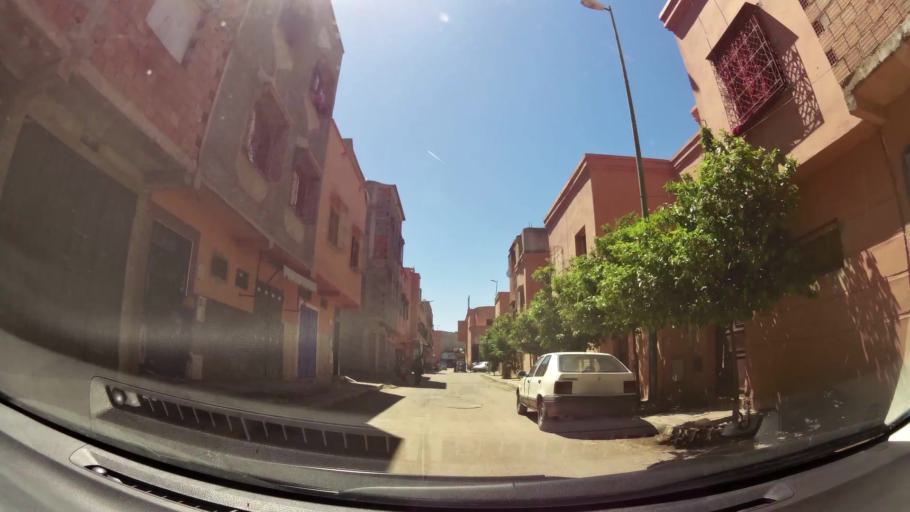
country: MA
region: Marrakech-Tensift-Al Haouz
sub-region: Marrakech
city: Marrakesh
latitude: 31.5732
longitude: -7.9828
